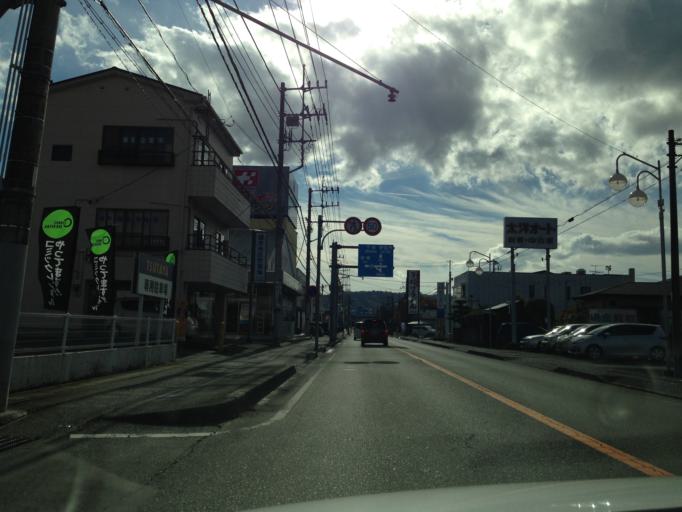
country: JP
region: Shizuoka
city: Mishima
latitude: 35.0131
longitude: 138.9439
